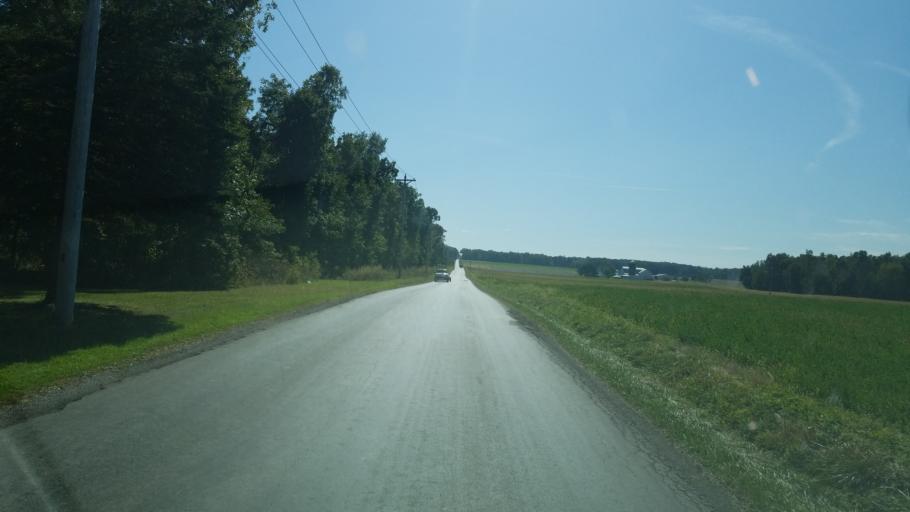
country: US
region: Ohio
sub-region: Wayne County
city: West Salem
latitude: 40.8543
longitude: -82.0739
